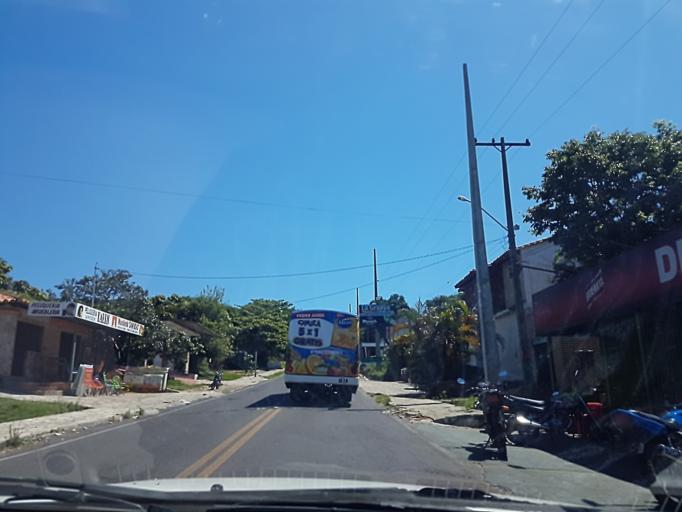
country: PY
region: Cordillera
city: Altos
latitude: -25.2582
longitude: -57.2465
